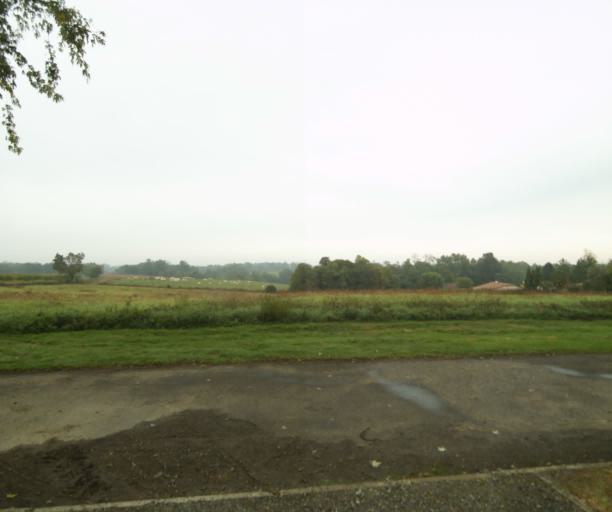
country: FR
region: Midi-Pyrenees
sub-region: Departement du Gers
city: Cazaubon
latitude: 43.9192
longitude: -0.1066
